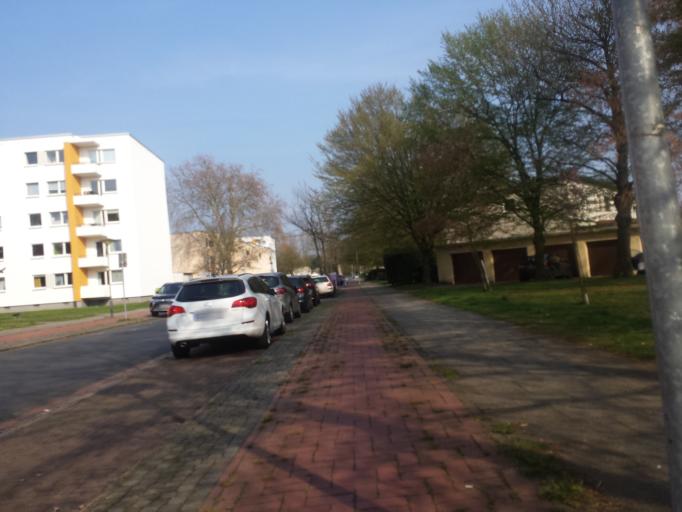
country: DE
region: Lower Saxony
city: Lilienthal
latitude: 53.0762
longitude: 8.9079
